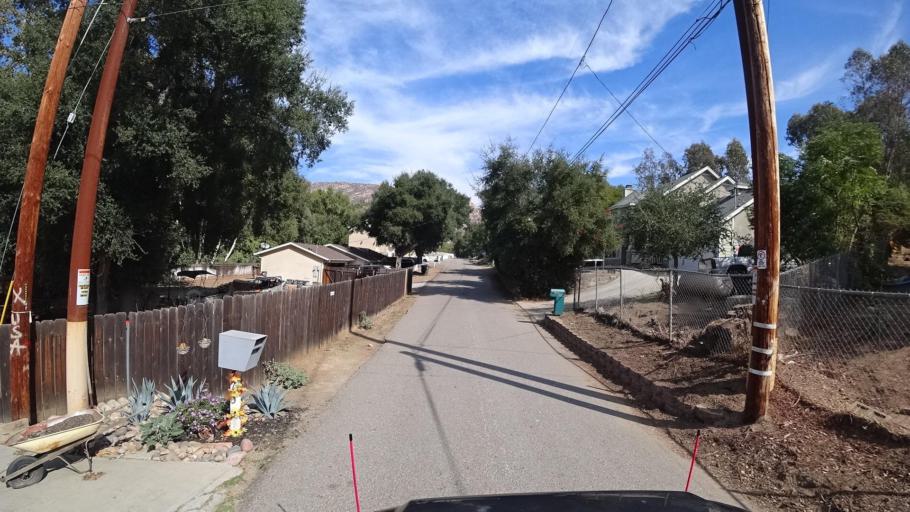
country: US
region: California
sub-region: San Diego County
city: Harbison Canyon
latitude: 32.8157
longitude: -116.8338
